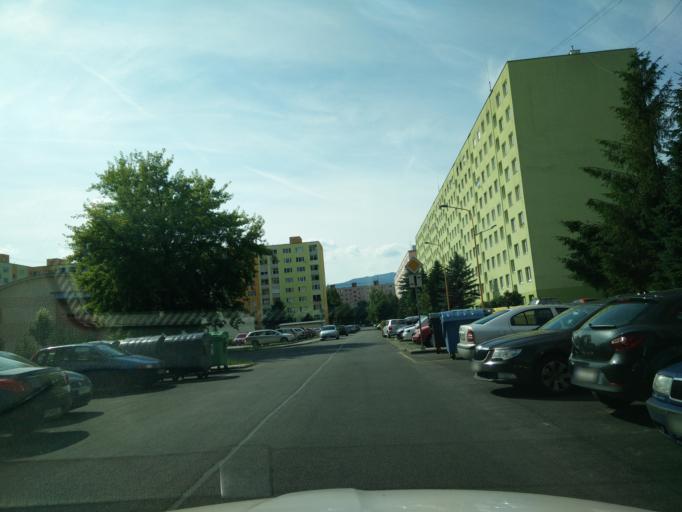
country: SK
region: Nitriansky
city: Prievidza
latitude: 48.7841
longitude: 18.6225
